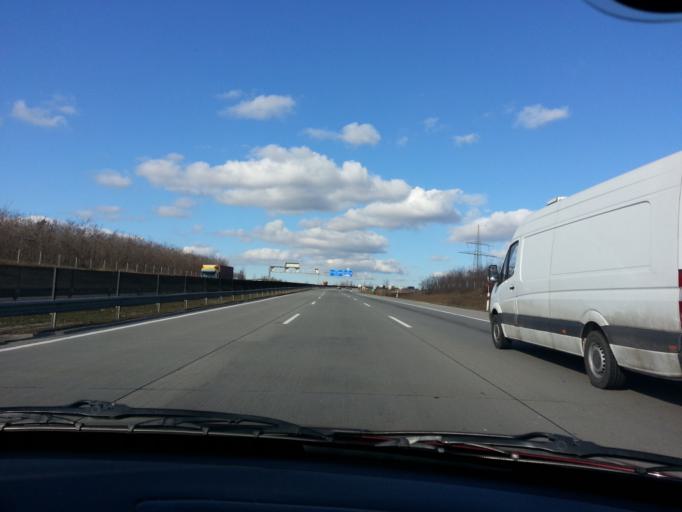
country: HU
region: Pest
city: Ecser
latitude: 47.4524
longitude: 19.3313
